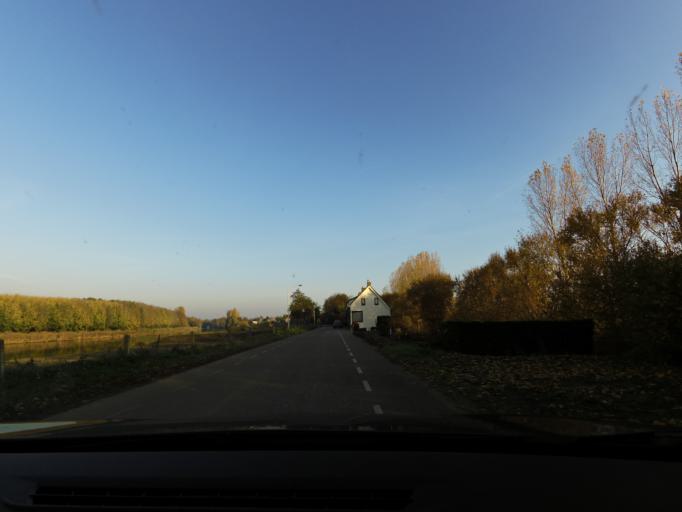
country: NL
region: North Brabant
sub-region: Gemeente Moerdijk
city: Klundert
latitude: 51.6065
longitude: 4.5079
